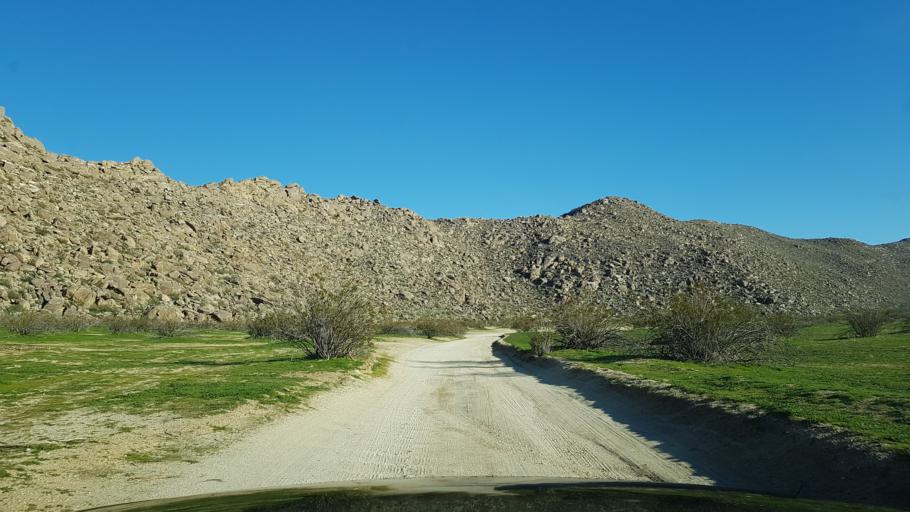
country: US
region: California
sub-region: San Diego County
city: Julian
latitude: 33.0288
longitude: -116.3970
